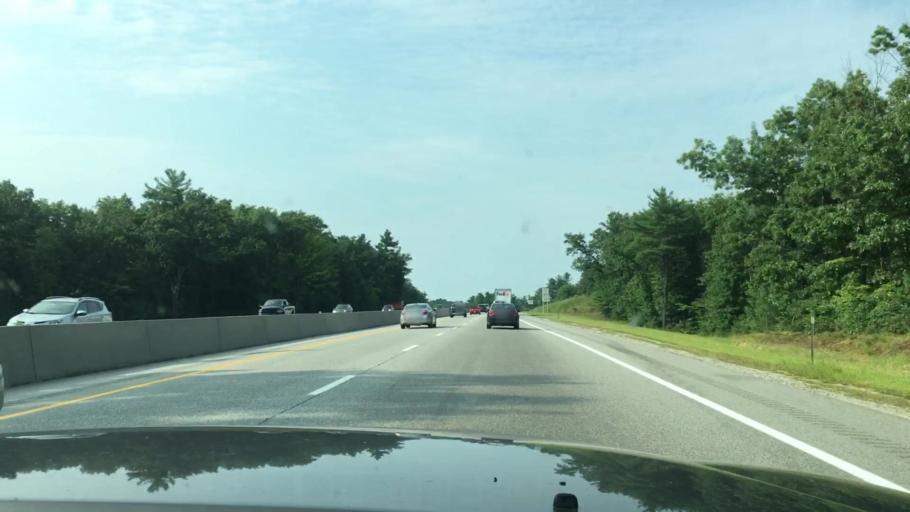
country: US
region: New Hampshire
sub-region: Hillsborough County
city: Merrimack
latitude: 42.8490
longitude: -71.4963
